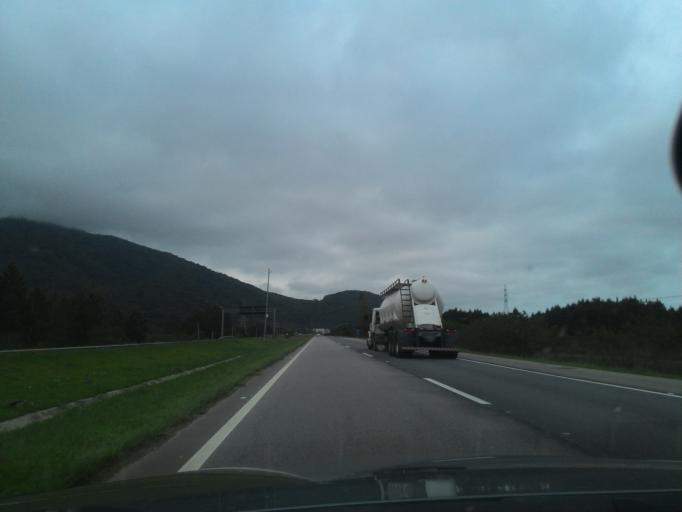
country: BR
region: Santa Catarina
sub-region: Florianopolis
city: Pantano do Sul
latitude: -27.8702
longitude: -48.6464
